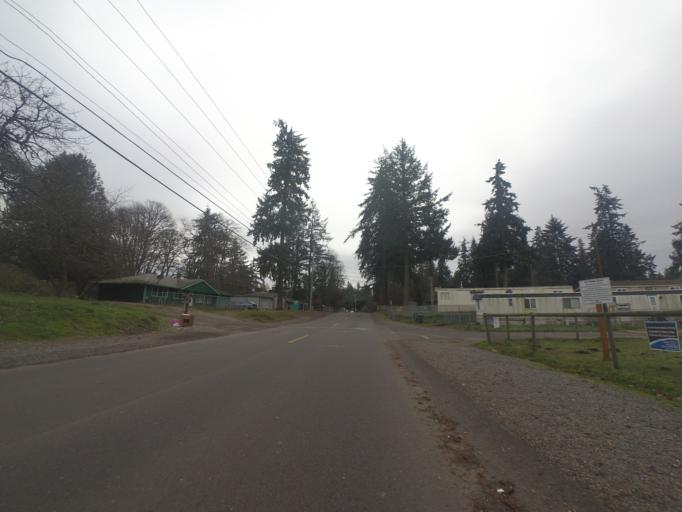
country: US
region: Washington
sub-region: Pierce County
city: McChord Air Force Base
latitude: 47.1231
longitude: -122.5270
